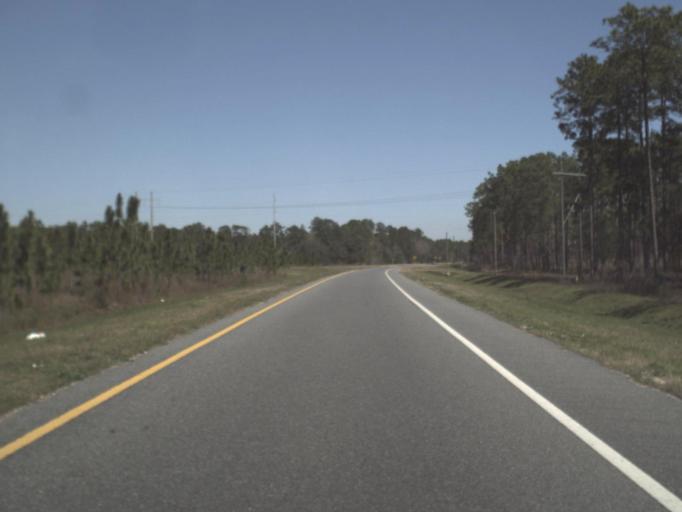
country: US
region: Florida
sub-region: Leon County
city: Woodville
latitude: 30.3466
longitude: -84.3097
